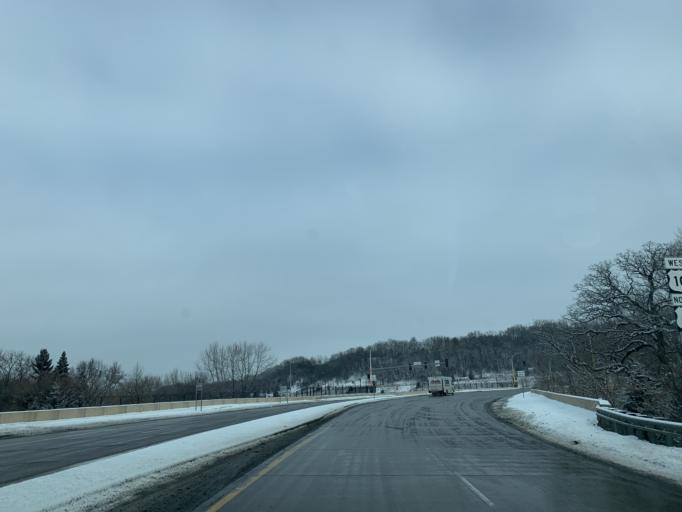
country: US
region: Minnesota
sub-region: Washington County
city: Saint Paul Park
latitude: 44.8493
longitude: -92.9914
